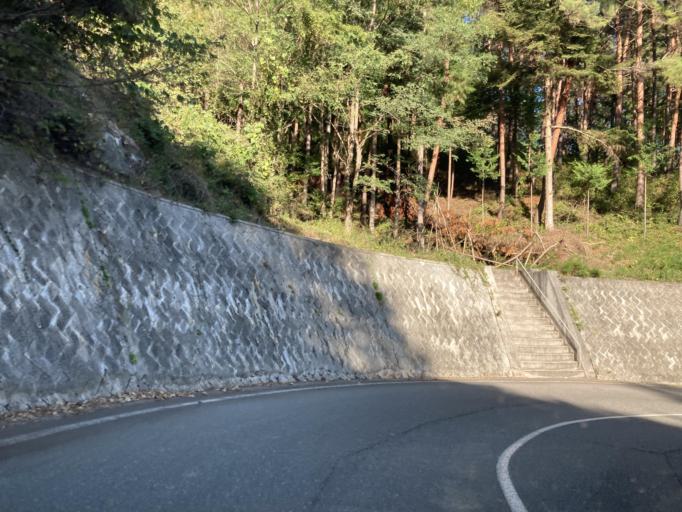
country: JP
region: Nagano
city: Omachi
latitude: 36.4883
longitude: 137.9033
